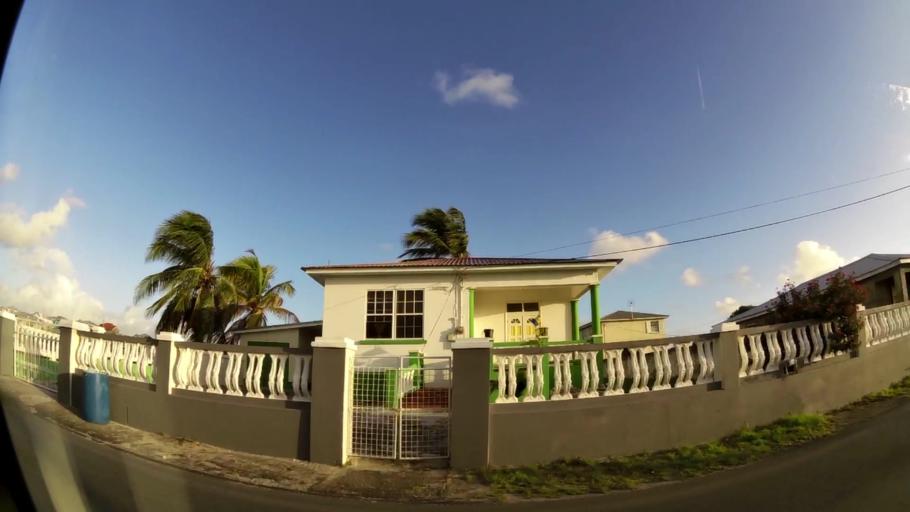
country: BB
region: Christ Church
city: Oistins
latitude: 13.0806
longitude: -59.4977
